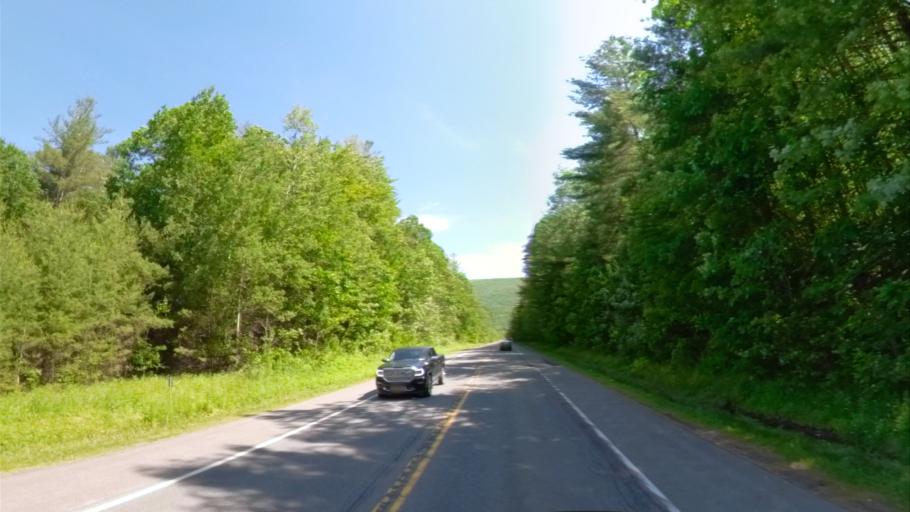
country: US
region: New York
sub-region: Ulster County
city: Shokan
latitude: 42.1059
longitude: -74.4325
